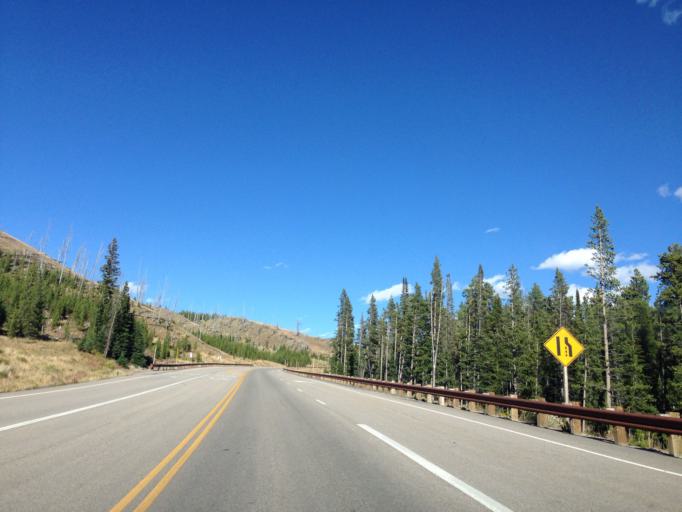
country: US
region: Montana
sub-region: Stillwater County
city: Absarokee
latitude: 45.0243
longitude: -109.9163
